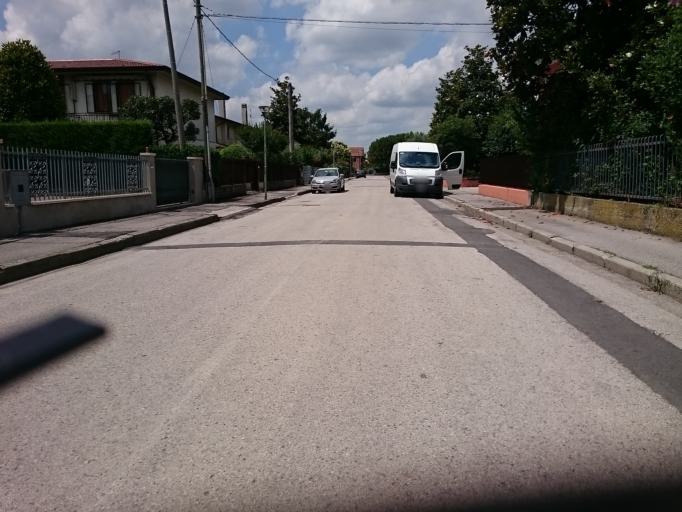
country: IT
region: Veneto
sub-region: Provincia di Padova
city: Caselle
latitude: 45.4105
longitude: 11.8229
